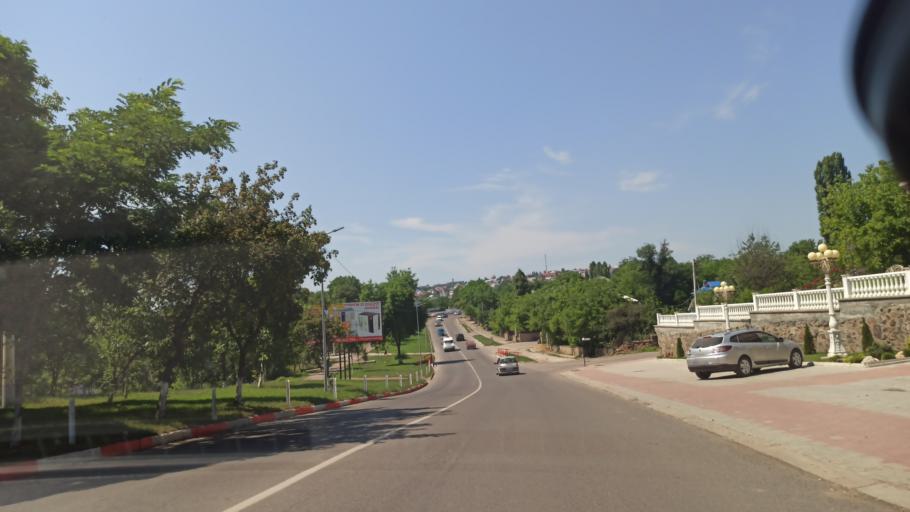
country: MD
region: Raionul Soroca
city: Soroca
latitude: 48.1698
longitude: 28.3087
